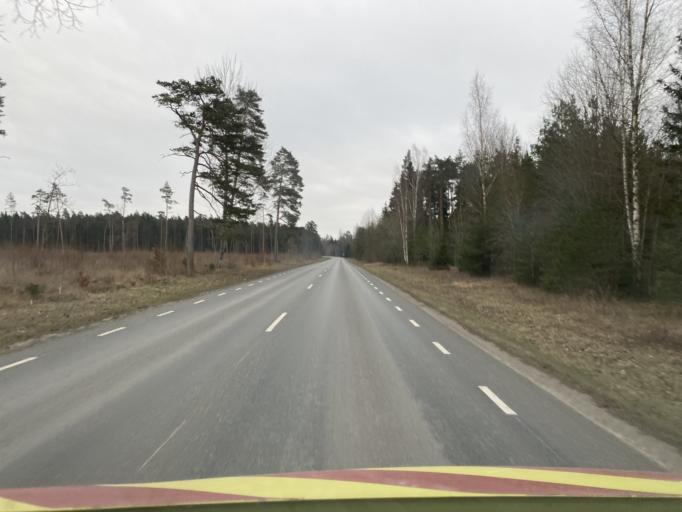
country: EE
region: Laeaene
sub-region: Ridala Parish
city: Uuemoisa
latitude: 59.0067
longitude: 23.6935
